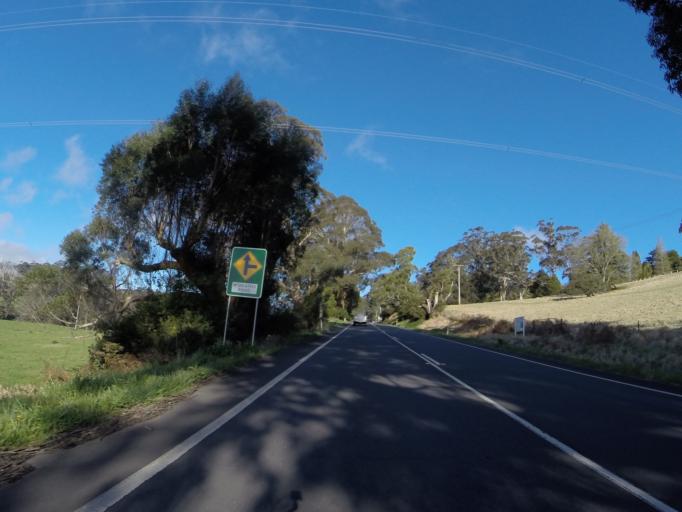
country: AU
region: New South Wales
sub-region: Shoalhaven Shire
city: Kangaroo Valley
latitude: -34.5866
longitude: 150.5397
